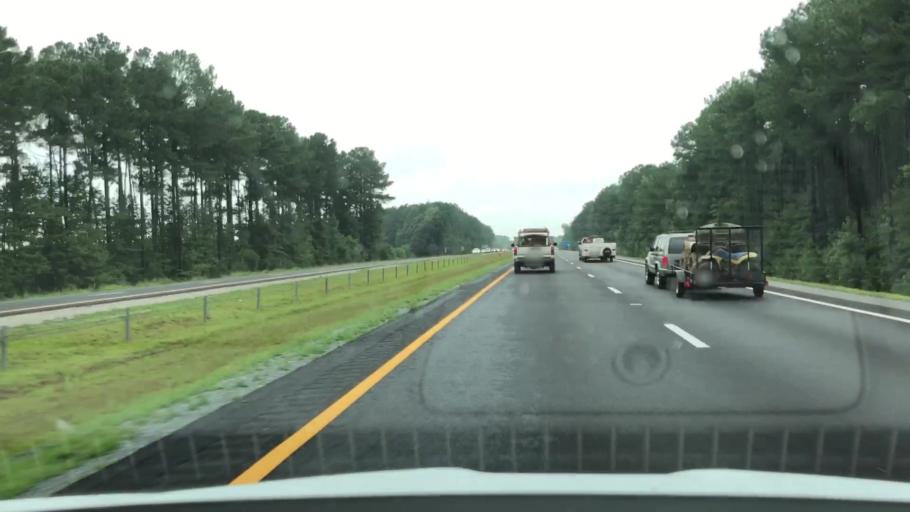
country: US
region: North Carolina
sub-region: Wayne County
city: Fremont
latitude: 35.4833
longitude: -77.9905
